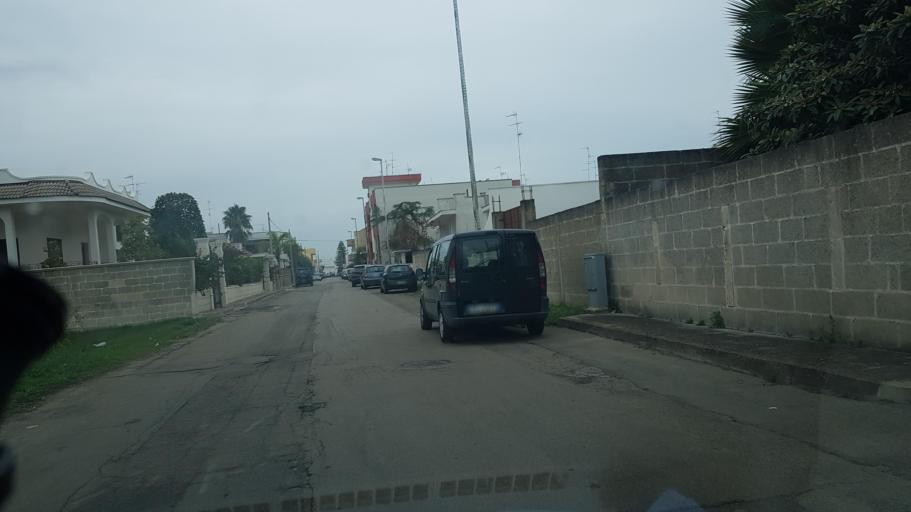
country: IT
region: Apulia
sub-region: Provincia di Lecce
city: Veglie
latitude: 40.3339
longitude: 17.9588
